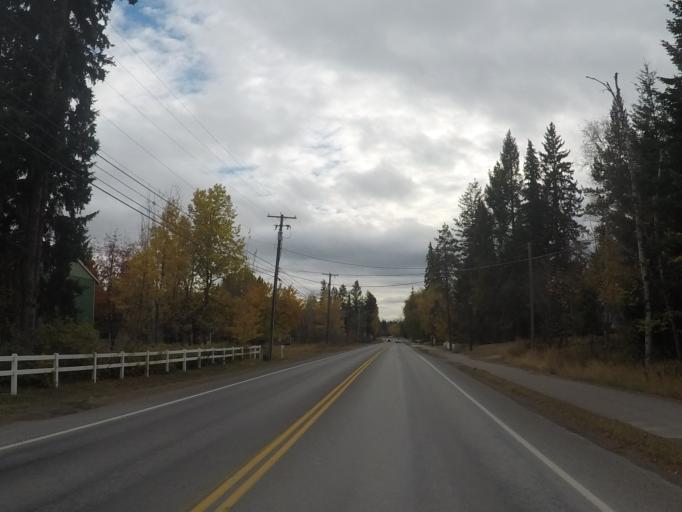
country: US
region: Montana
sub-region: Flathead County
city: Whitefish
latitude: 48.4202
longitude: -114.3412
